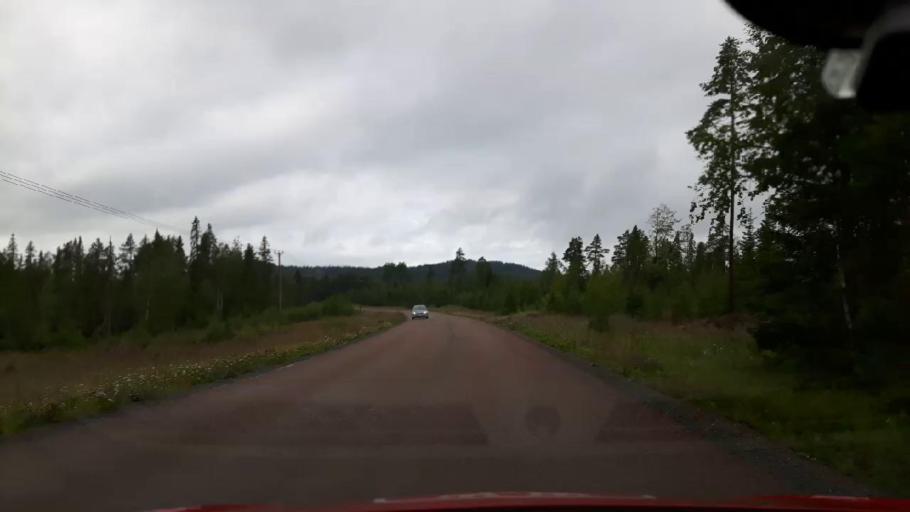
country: SE
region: Jaemtland
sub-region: Krokoms Kommun
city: Krokom
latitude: 63.3589
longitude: 14.1142
